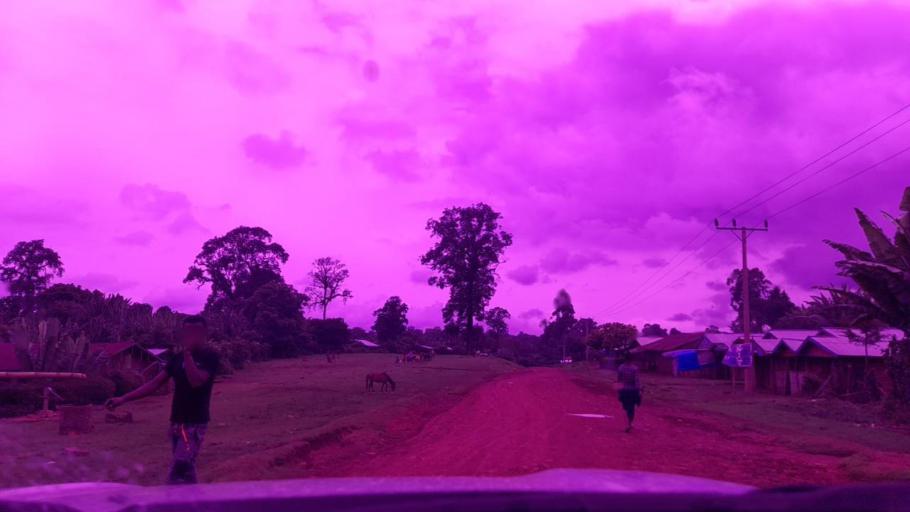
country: ET
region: Southern Nations, Nationalities, and People's Region
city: Tippi
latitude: 7.5804
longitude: 35.6309
